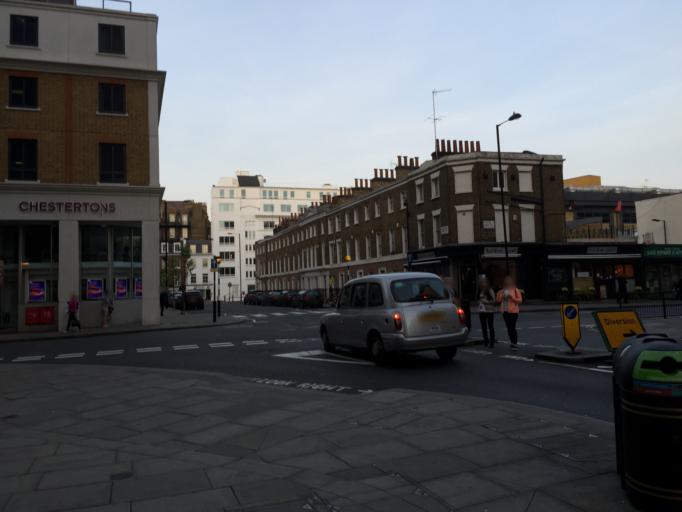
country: GB
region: England
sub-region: Greater London
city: London
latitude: 51.4937
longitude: -0.1420
